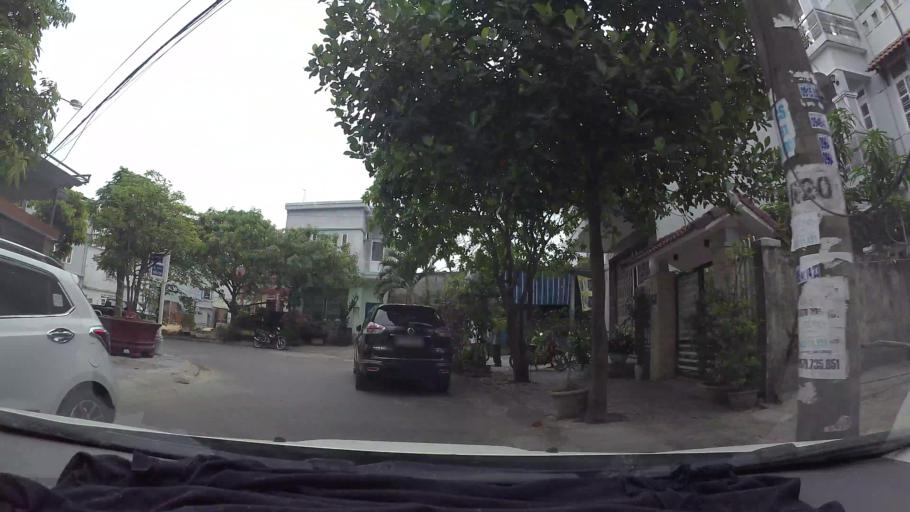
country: VN
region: Da Nang
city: Lien Chieu
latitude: 16.0577
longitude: 108.1707
